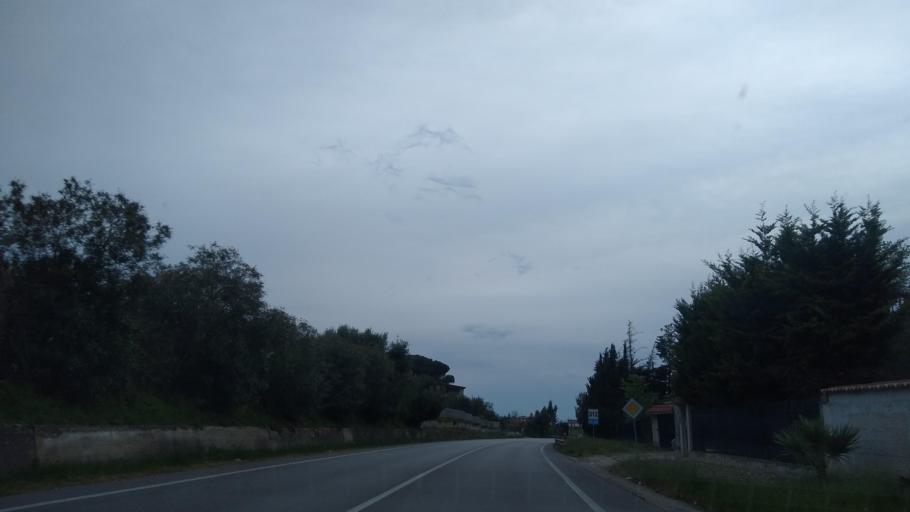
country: IT
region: Sicily
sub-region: Palermo
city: Partinico
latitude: 38.0271
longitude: 13.0893
